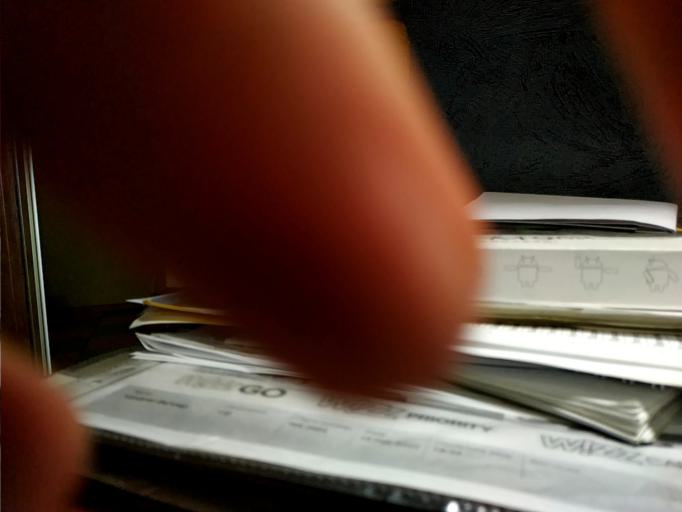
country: RU
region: Novgorod
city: Kholm
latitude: 57.1182
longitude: 31.4774
